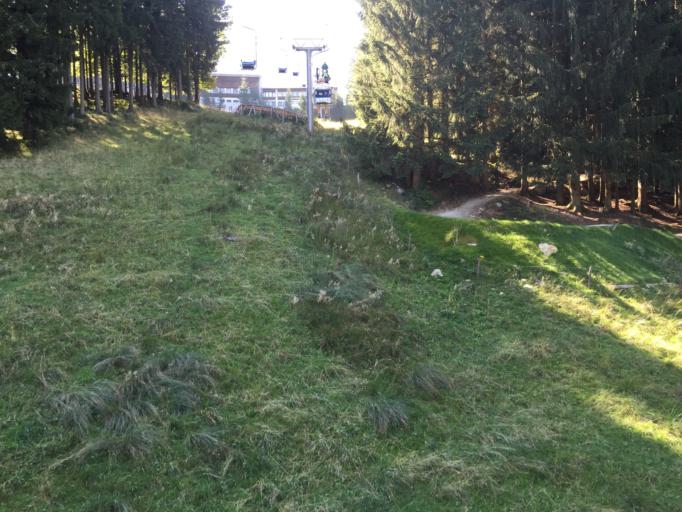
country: DE
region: Bavaria
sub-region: Upper Bavaria
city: Samerberg
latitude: 47.7624
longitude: 12.2389
